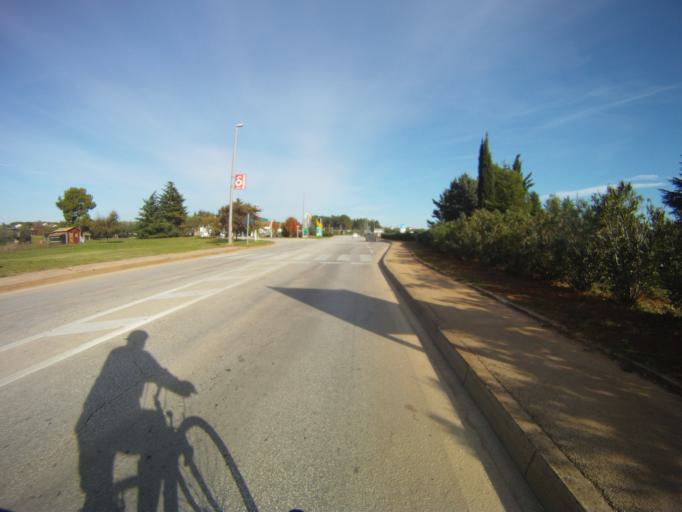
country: HR
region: Istarska
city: Novigrad
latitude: 45.3183
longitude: 13.5733
